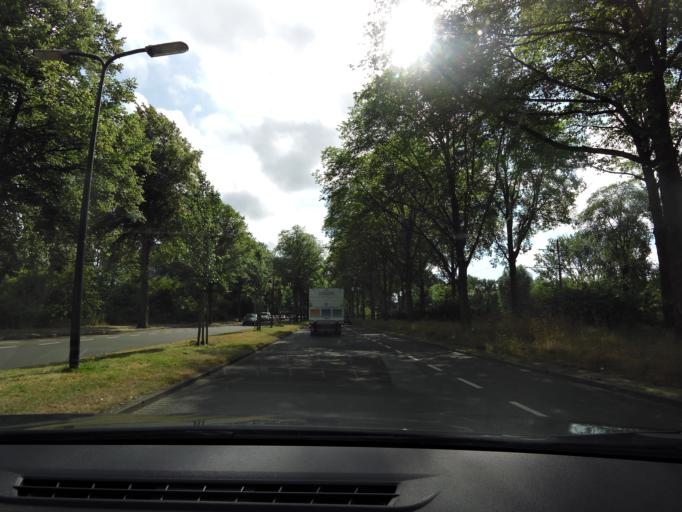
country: NL
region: South Holland
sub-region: Gemeente Westland
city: Kwintsheul
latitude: 52.0426
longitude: 4.2728
